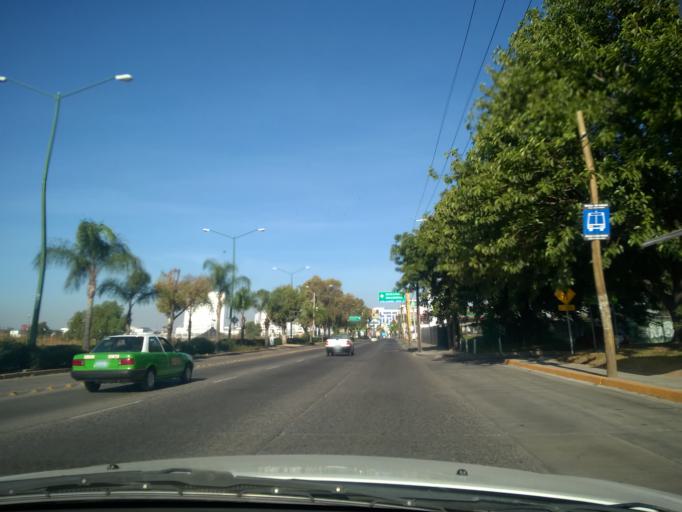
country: MX
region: Guanajuato
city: Leon
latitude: 21.1114
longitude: -101.6475
